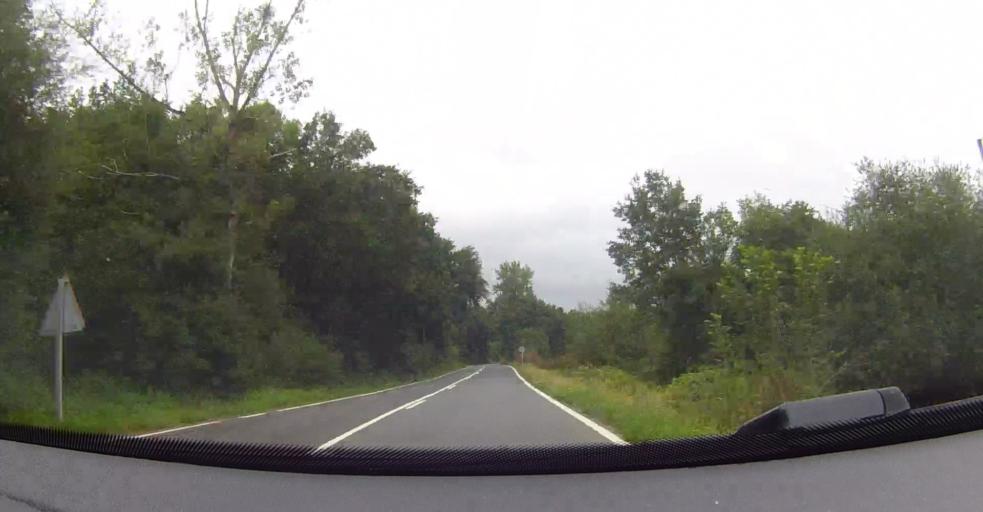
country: ES
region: Basque Country
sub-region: Bizkaia
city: Lanestosa
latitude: 43.2405
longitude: -3.3216
